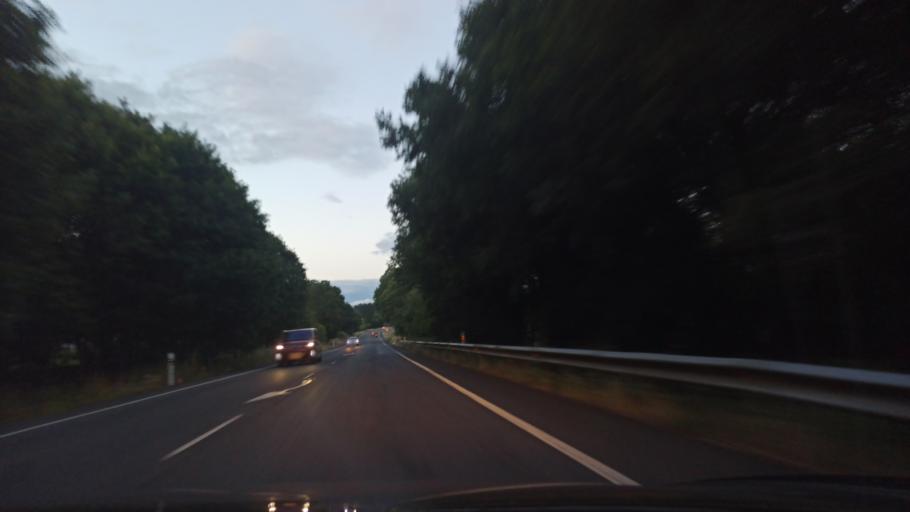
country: ES
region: Galicia
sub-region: Provincia de Lugo
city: Ourol
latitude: 42.9514
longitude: -7.6168
